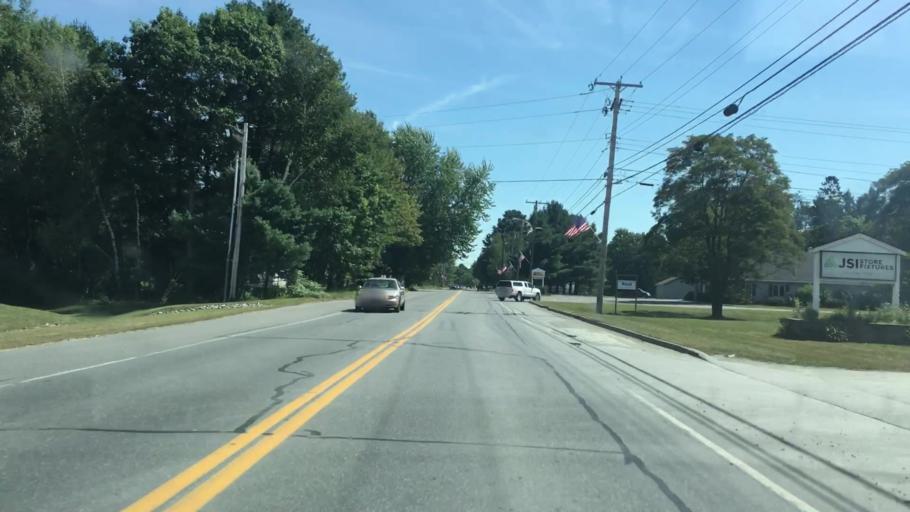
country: US
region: Maine
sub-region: Piscataquis County
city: Milo
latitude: 45.2638
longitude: -68.9915
